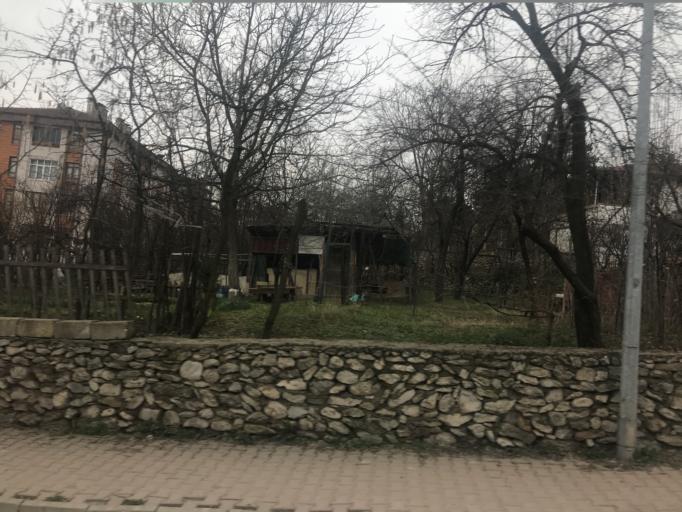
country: TR
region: Karabuk
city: Safranbolu
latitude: 41.2593
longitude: 32.6793
